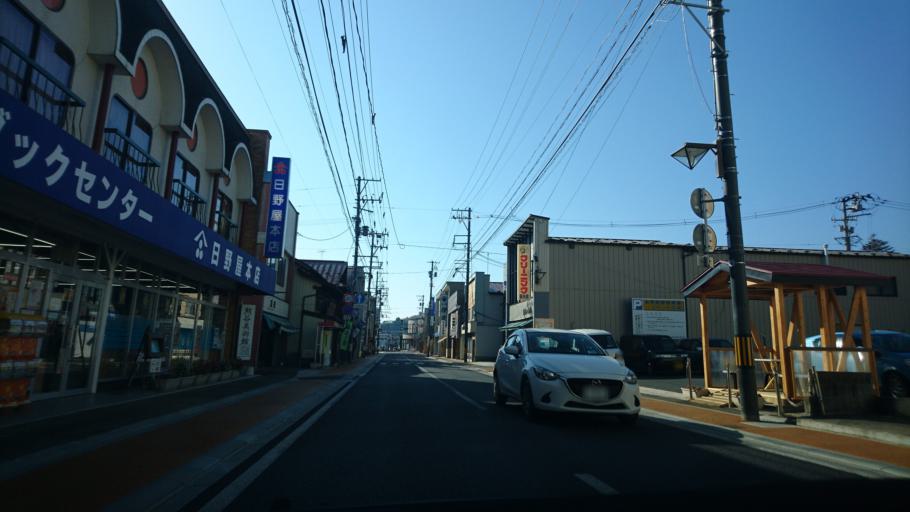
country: JP
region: Iwate
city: Ichinoseki
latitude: 38.9195
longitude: 141.3349
